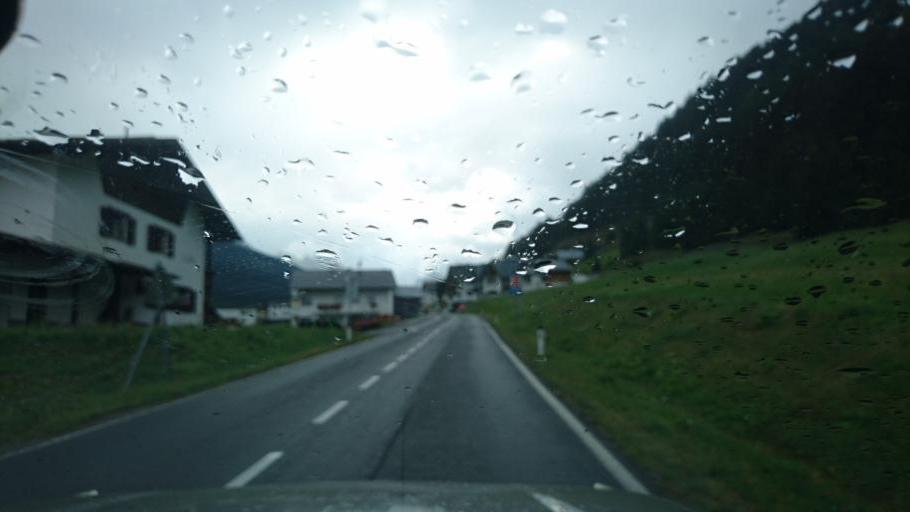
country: AT
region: Tyrol
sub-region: Politischer Bezirk Landeck
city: Ischgl
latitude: 46.9911
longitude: 10.2515
